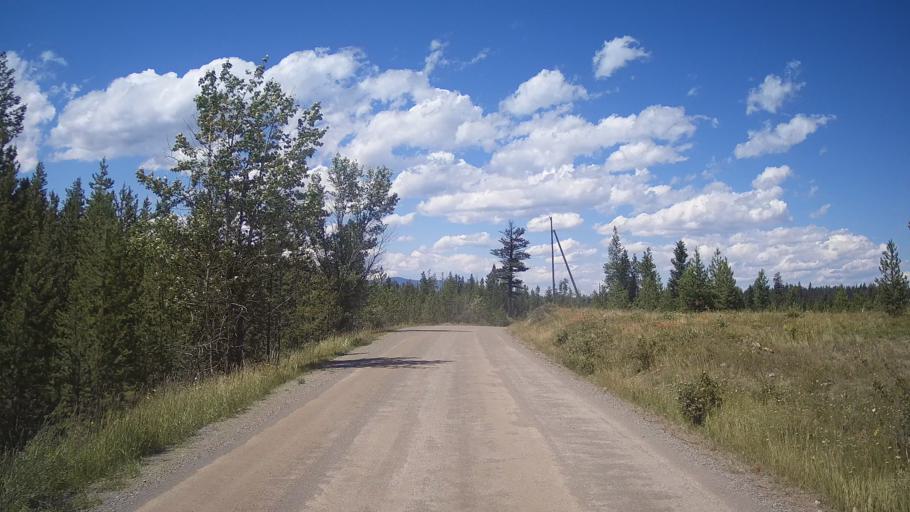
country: CA
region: British Columbia
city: Cache Creek
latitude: 51.2242
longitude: -121.6216
